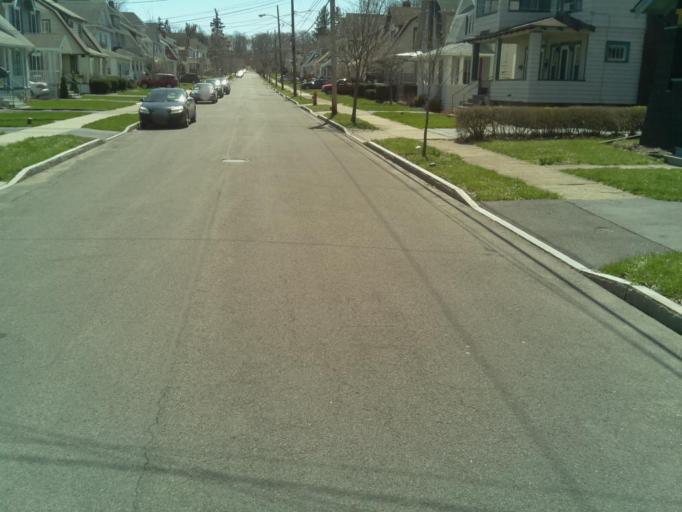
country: US
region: New York
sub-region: Onondaga County
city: Lyncourt
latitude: 43.0672
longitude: -76.1167
